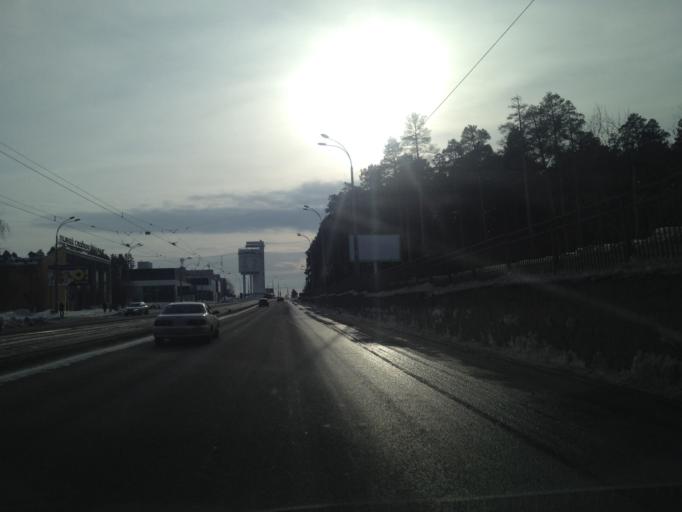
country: RU
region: Sverdlovsk
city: Yekaterinburg
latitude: 56.8962
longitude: 60.5759
